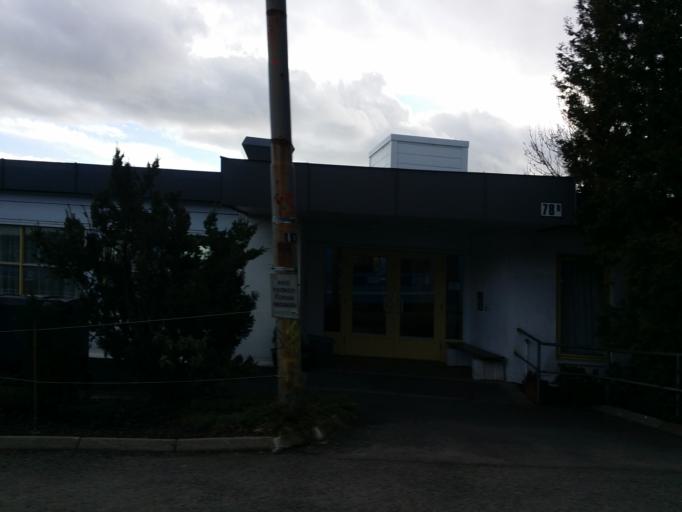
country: NO
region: Oslo
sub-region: Oslo
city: Oslo
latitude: 59.9513
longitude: 10.7863
